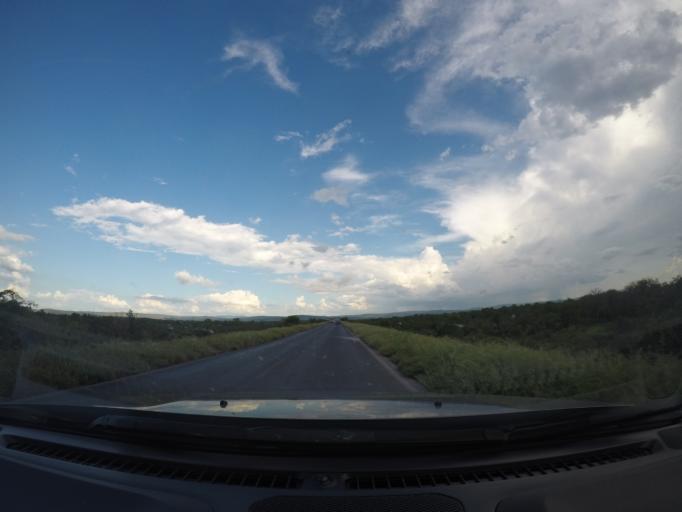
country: BR
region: Bahia
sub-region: Ibotirama
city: Ibotirama
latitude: -12.1665
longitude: -43.2757
